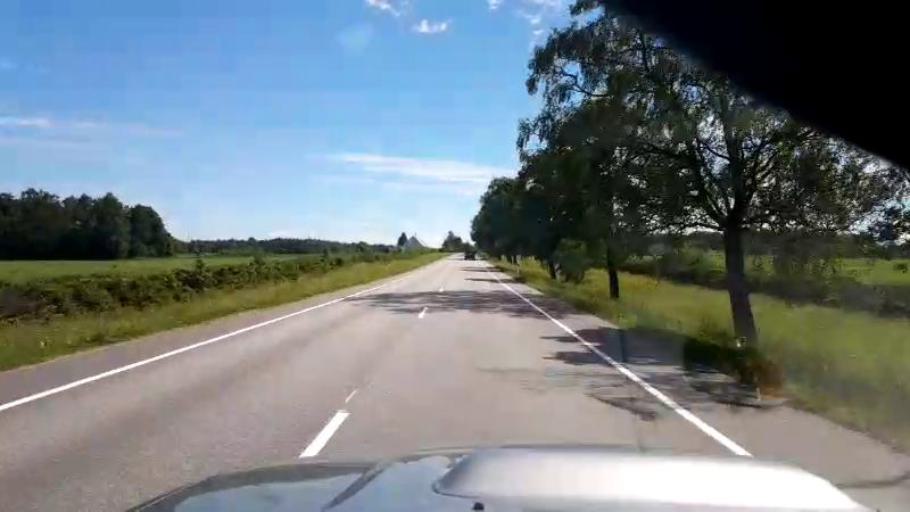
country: EE
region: Jaervamaa
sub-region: Jaerva-Jaani vald
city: Jarva-Jaani
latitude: 59.0073
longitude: 25.9277
